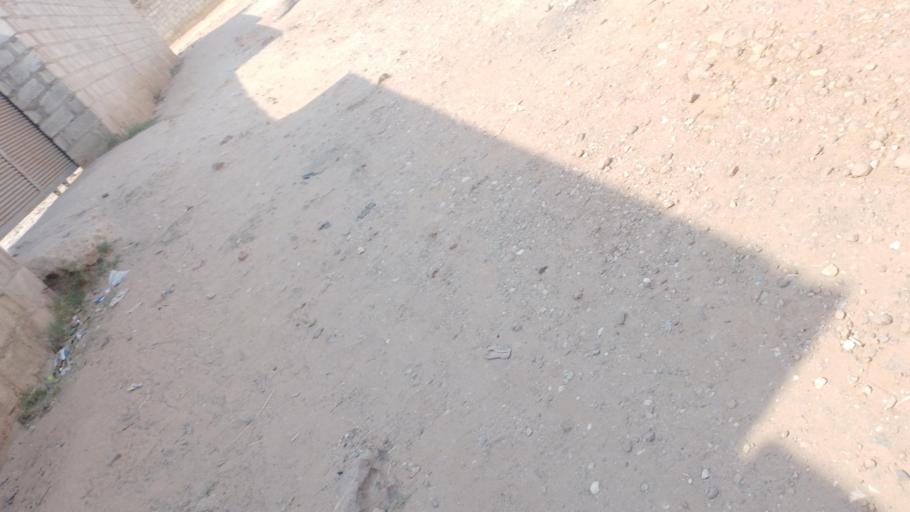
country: ZM
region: Lusaka
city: Lusaka
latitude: -15.4079
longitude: 28.3798
